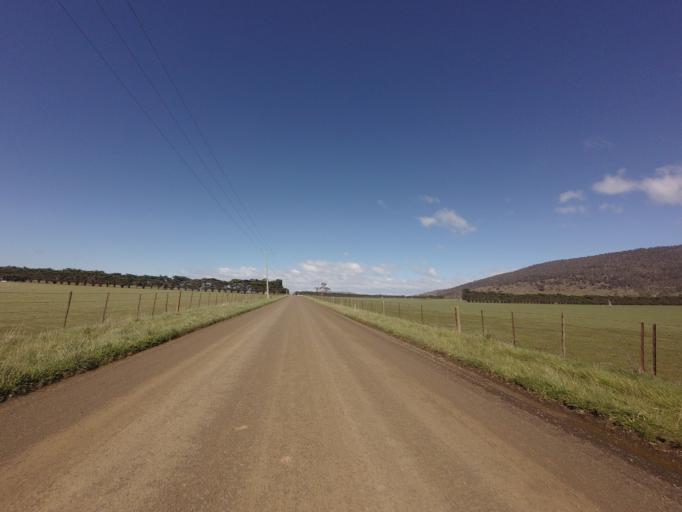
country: AU
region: Tasmania
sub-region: Northern Midlands
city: Evandale
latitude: -41.9599
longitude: 147.4380
